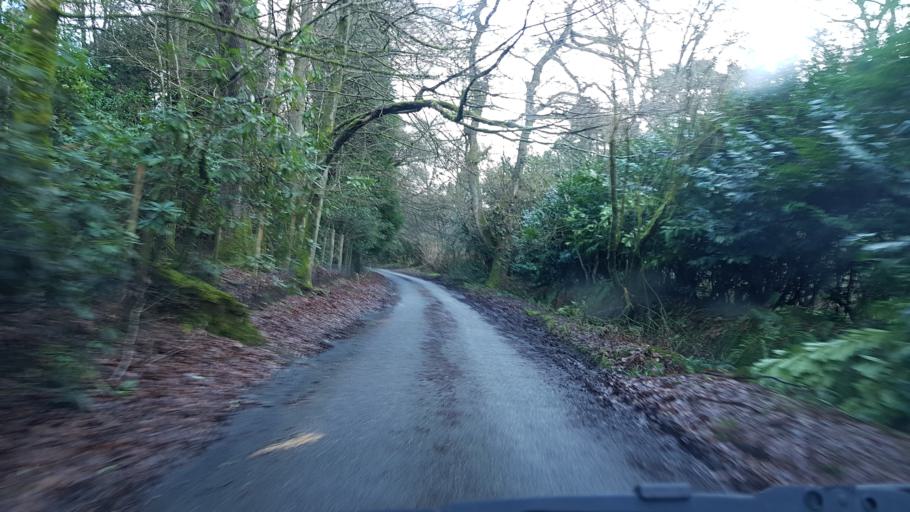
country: GB
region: England
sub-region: Surrey
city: Churt
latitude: 51.1086
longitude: -0.7709
